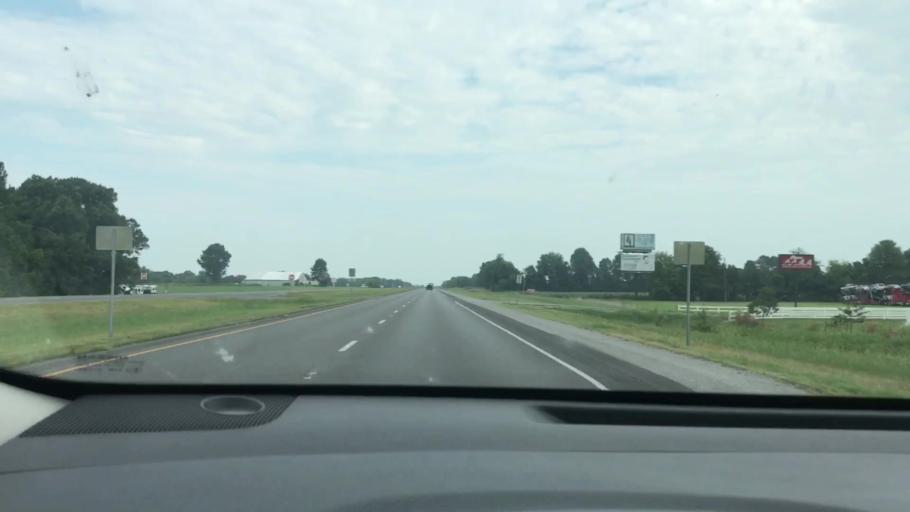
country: US
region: Kentucky
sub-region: Calloway County
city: Murray
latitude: 36.6863
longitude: -88.3028
